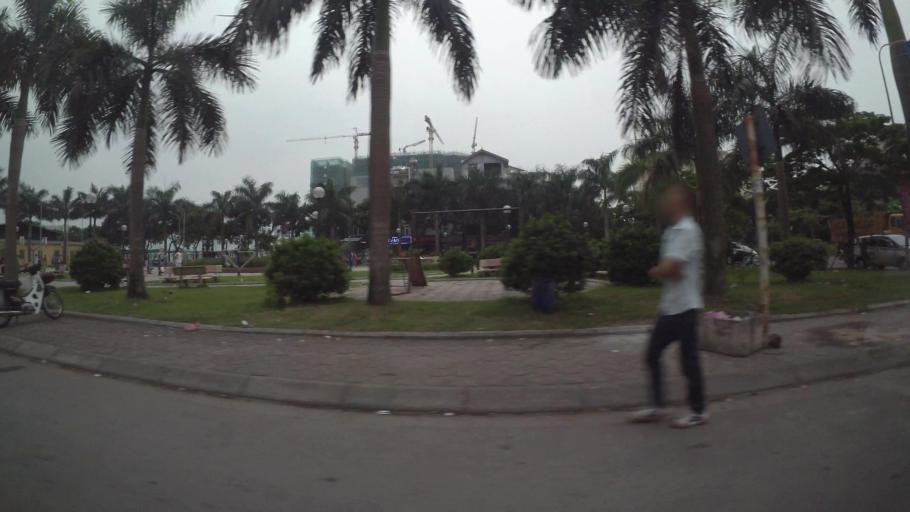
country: VN
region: Ha Noi
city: Trau Quy
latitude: 21.0392
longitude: 105.9035
